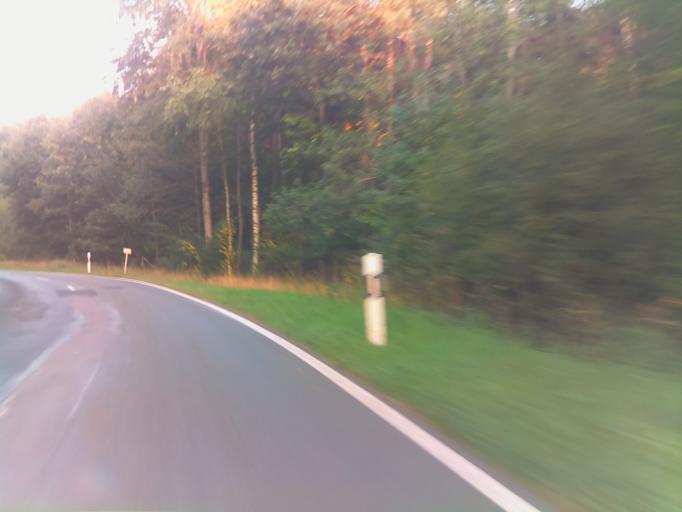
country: DE
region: Bavaria
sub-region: Regierungsbezirk Unterfranken
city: Wartmannsroth
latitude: 50.1491
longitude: 9.7982
